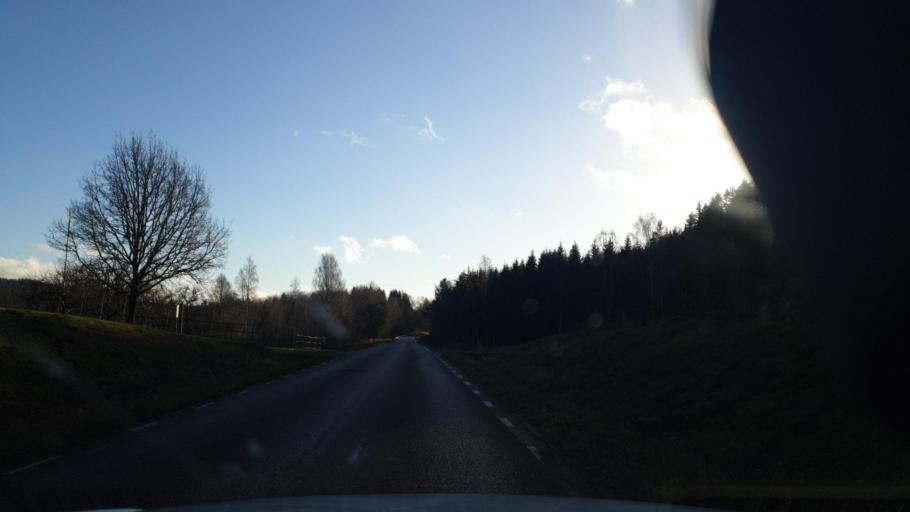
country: NO
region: Hedmark
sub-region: Eidskog
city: Skotterud
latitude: 59.7626
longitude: 12.0497
